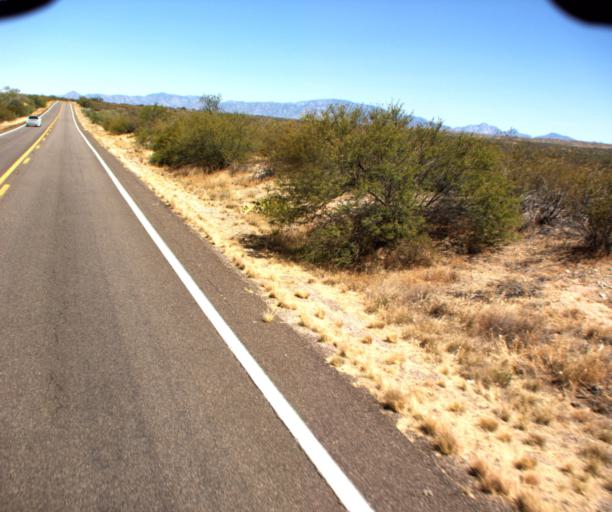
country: US
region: Arizona
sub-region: Pima County
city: Catalina
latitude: 32.6481
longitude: -111.0265
